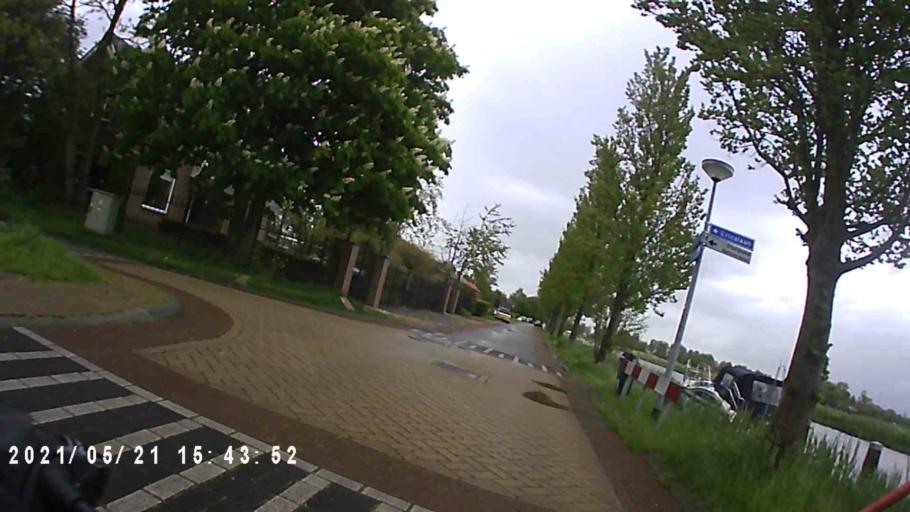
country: NL
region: Groningen
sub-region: Gemeente Zuidhorn
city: Aduard
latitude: 53.2008
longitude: 6.4490
